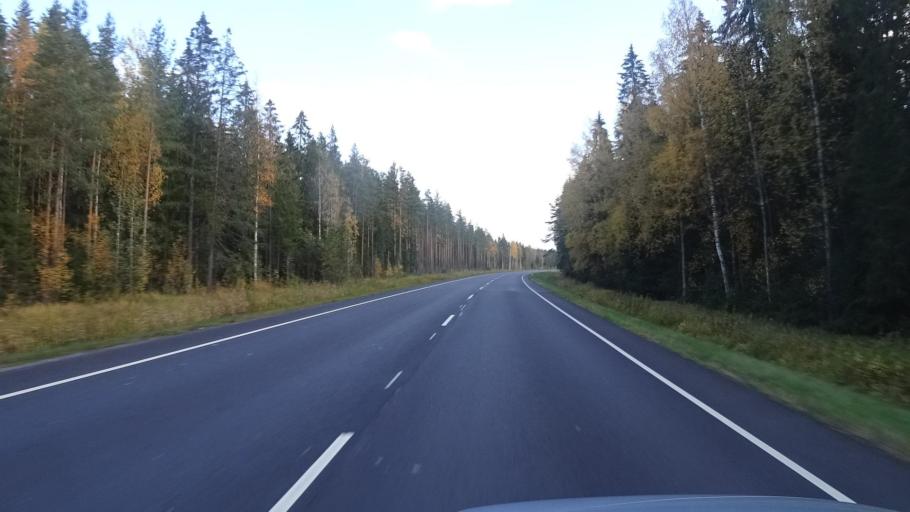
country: FI
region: Satakunta
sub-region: Rauma
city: Koeylioe
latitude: 61.1038
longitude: 22.2299
